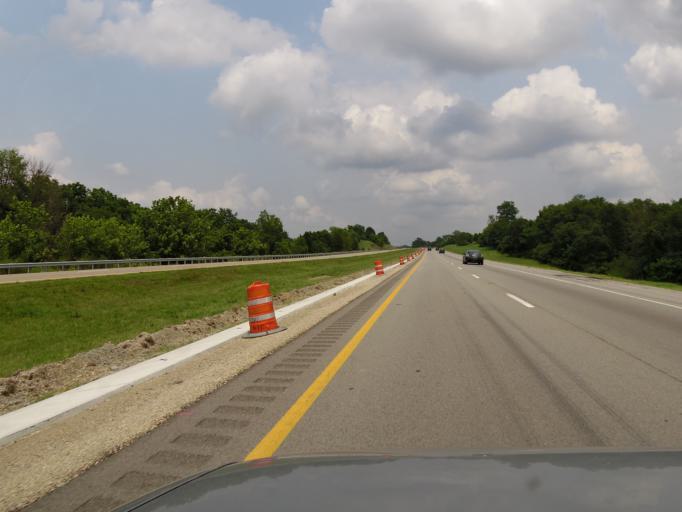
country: US
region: Indiana
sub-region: Switzerland County
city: Vevay
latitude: 38.6630
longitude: -85.0328
